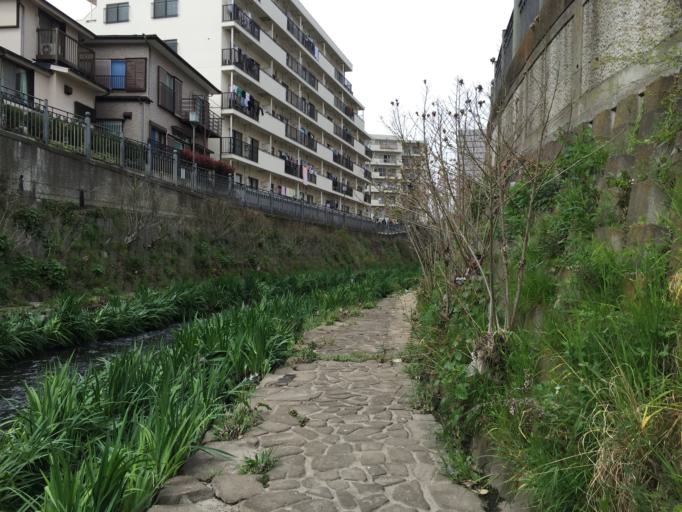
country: JP
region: Kanagawa
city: Yokohama
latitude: 35.4091
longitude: 139.5945
